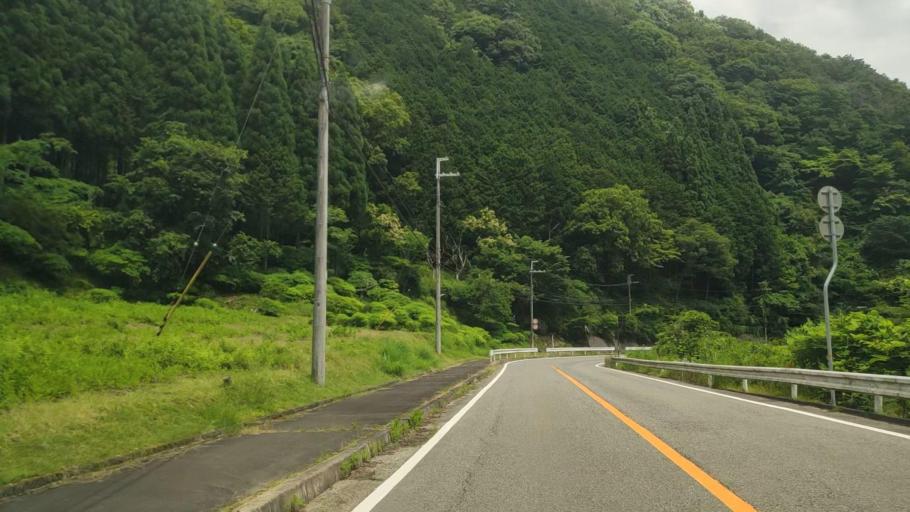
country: JP
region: Hyogo
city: Yamazakicho-nakabirose
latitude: 35.0938
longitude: 134.3613
